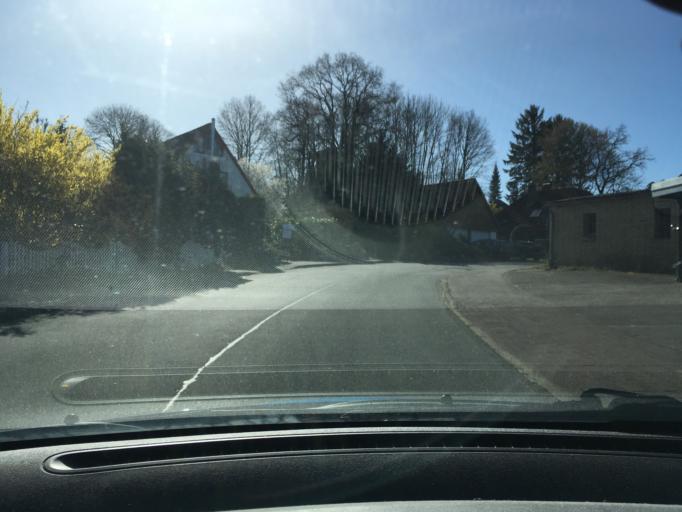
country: DE
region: Schleswig-Holstein
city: Fahrdorf
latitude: 54.5043
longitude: 9.5997
